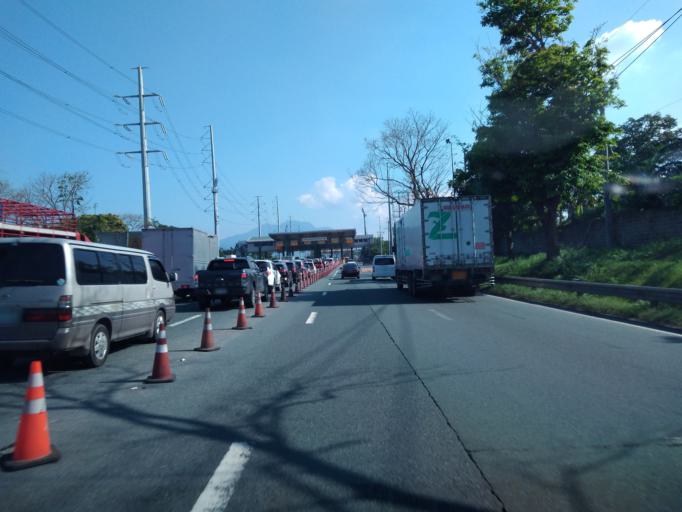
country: PH
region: Calabarzon
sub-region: Province of Laguna
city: Prinza
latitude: 14.2213
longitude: 121.1237
